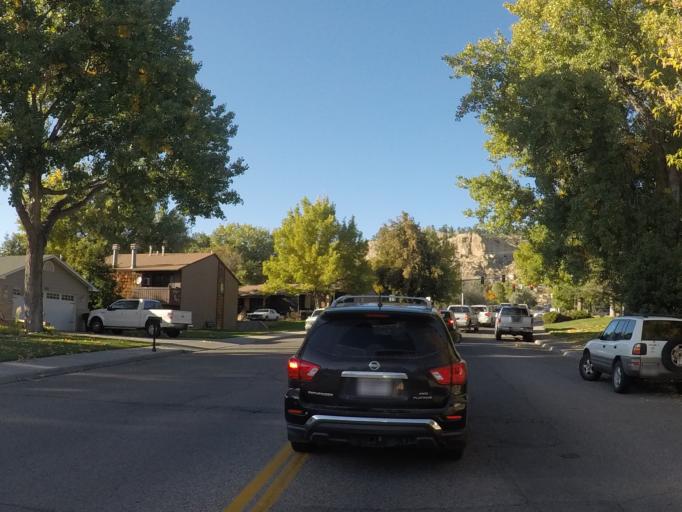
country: US
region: Montana
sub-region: Yellowstone County
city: Billings
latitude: 45.7976
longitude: -108.6018
